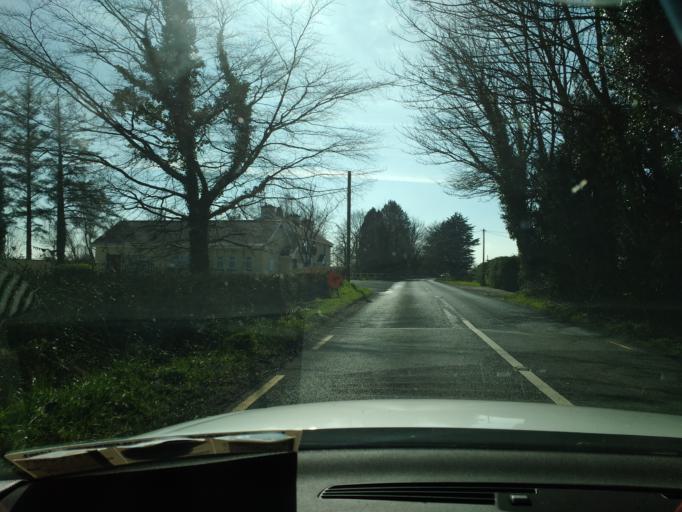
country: IE
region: Munster
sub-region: County Limerick
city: Castleconnell
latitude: 52.6989
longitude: -8.4608
